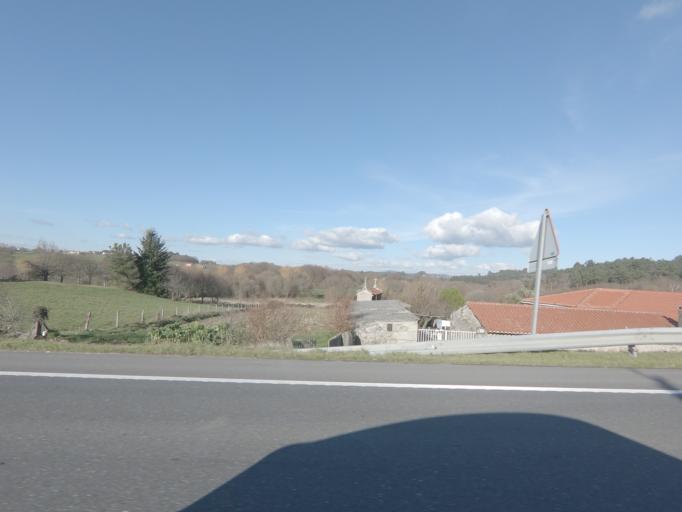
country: ES
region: Galicia
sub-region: Provincia de Pontevedra
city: Silleda
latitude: 42.7226
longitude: -8.2919
